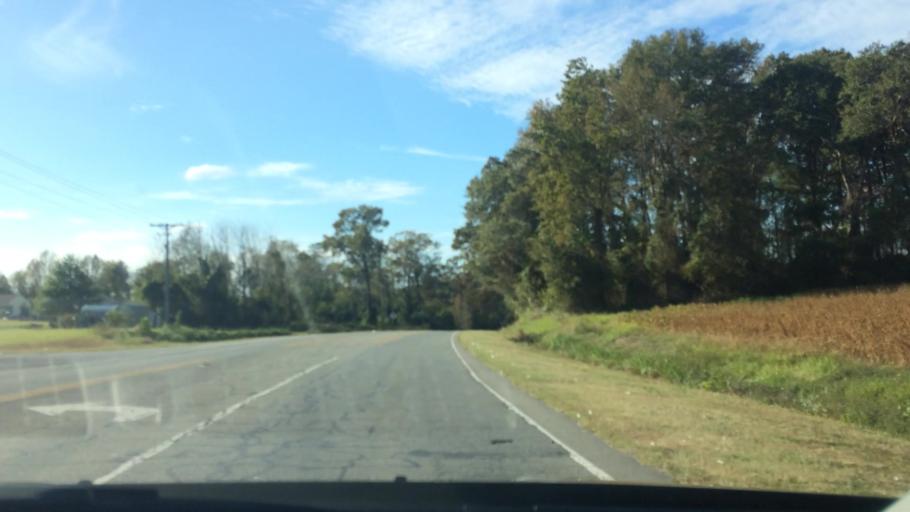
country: US
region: North Carolina
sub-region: Greene County
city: Snow Hill
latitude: 35.4564
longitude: -77.6947
